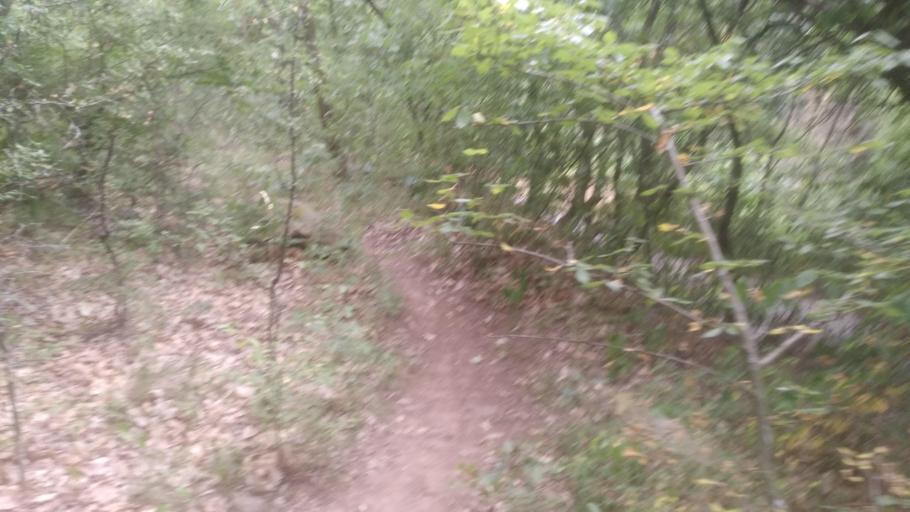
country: HU
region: Veszprem
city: Szentkiralyszabadja
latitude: 46.9994
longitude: 17.9736
